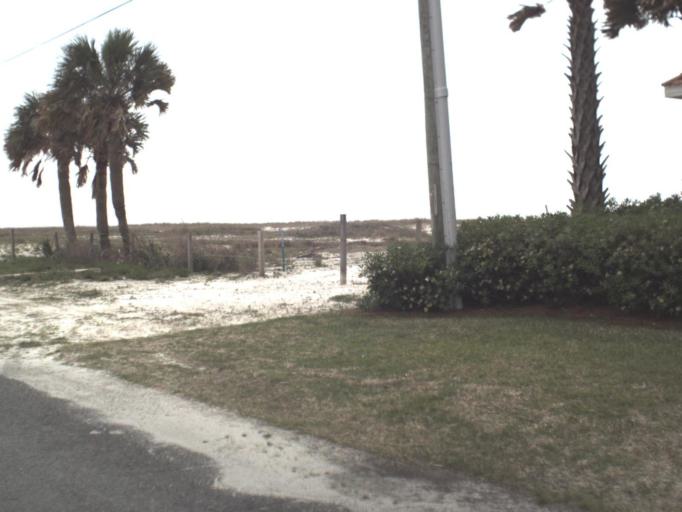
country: US
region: Alabama
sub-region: Baldwin County
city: Orange Beach
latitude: 30.2957
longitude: -87.4398
